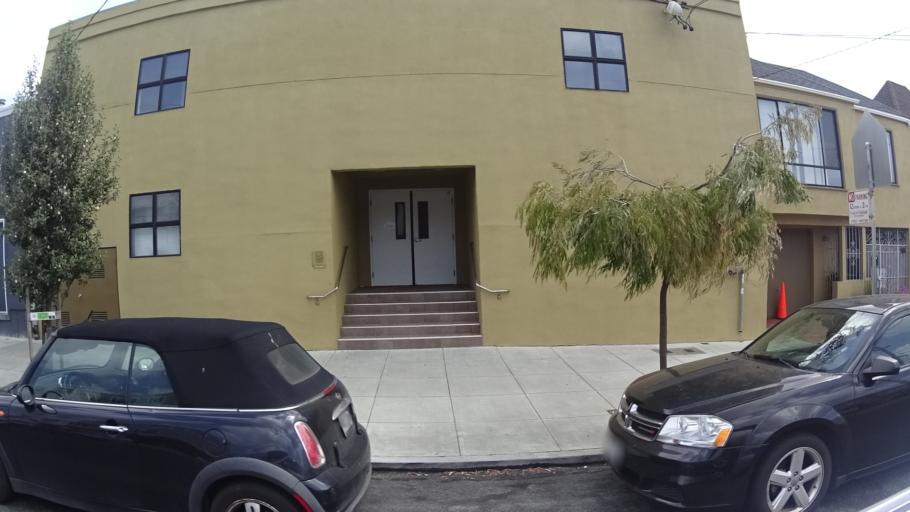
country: US
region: California
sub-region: San Mateo County
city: Daly City
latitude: 37.7565
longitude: -122.5024
